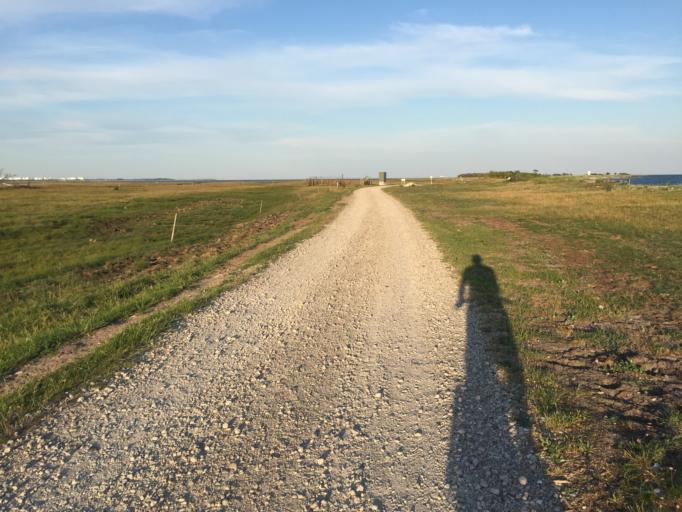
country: DK
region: Zealand
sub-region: Slagelse Kommune
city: Skaelskor
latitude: 55.1939
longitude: 11.1904
